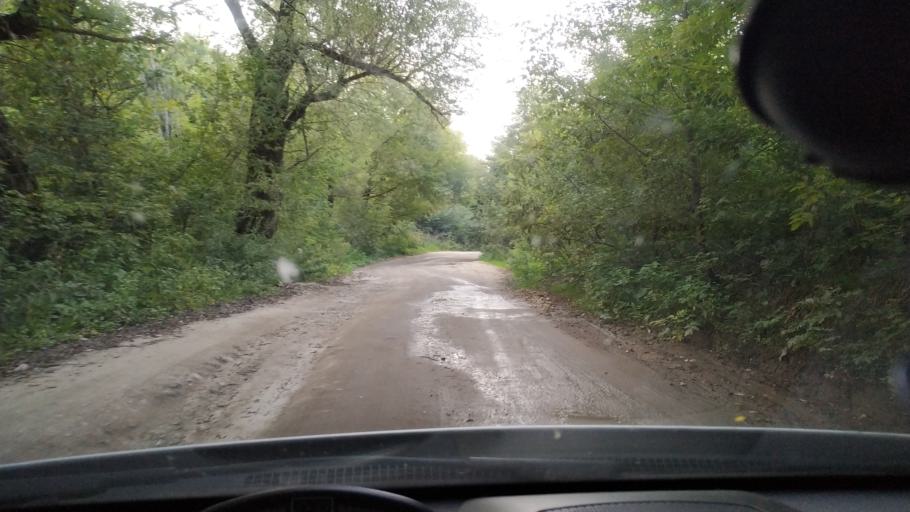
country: RU
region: Rjazan
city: Rybnoye
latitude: 54.8689
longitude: 39.6530
